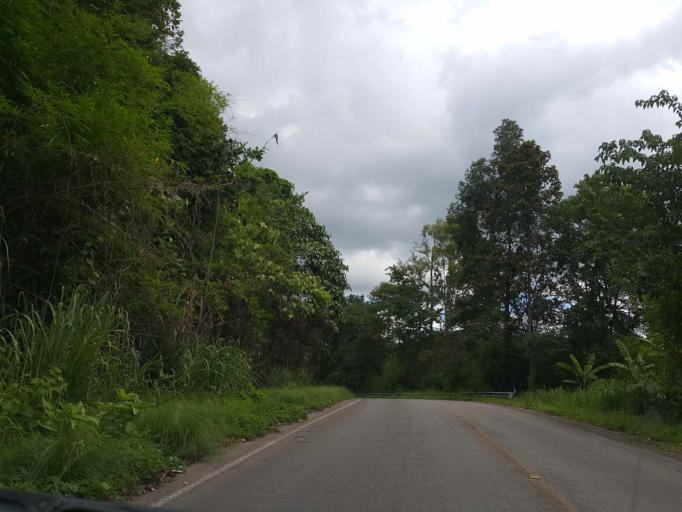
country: TH
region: Chiang Mai
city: Samoeng
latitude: 18.8088
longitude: 98.8186
